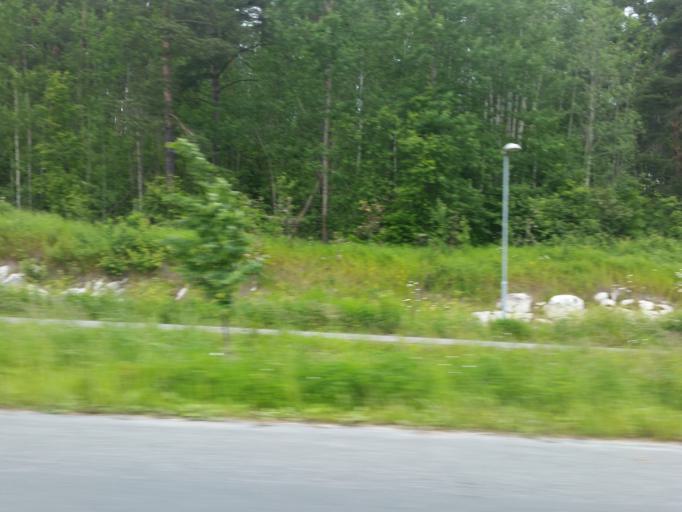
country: FI
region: Northern Savo
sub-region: Kuopio
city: Kuopio
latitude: 62.8819
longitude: 27.6530
